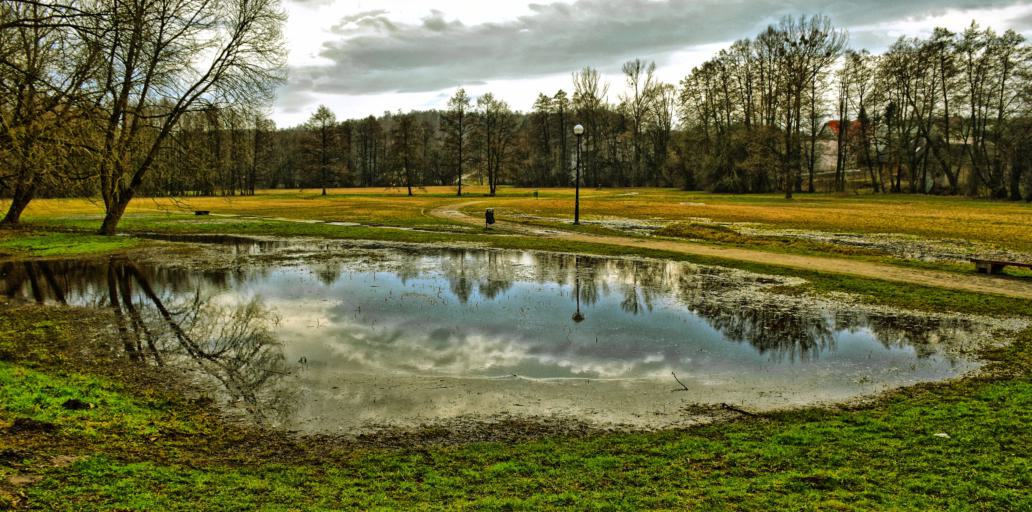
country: PL
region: Lublin Voivodeship
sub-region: Powiat pulawski
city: Naleczow
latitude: 51.2873
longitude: 22.2052
